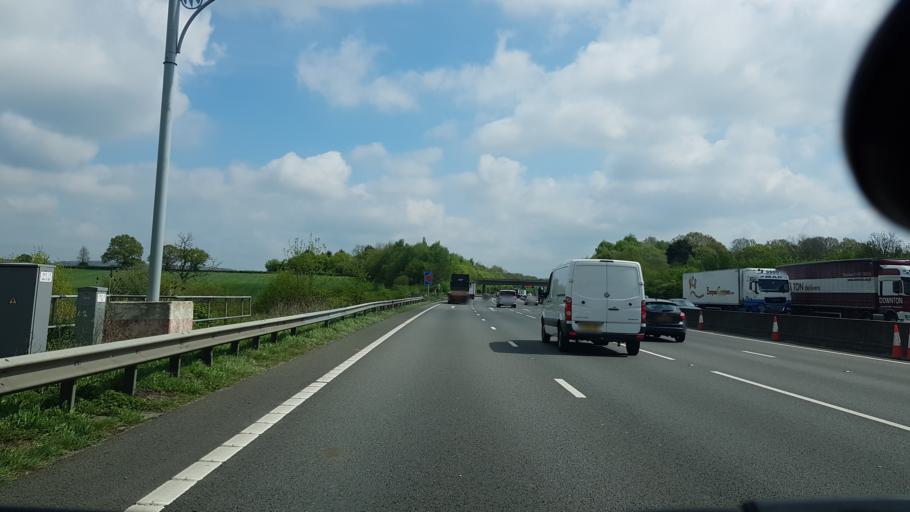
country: GB
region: England
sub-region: Kent
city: Westerham
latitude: 51.2844
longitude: 0.1064
